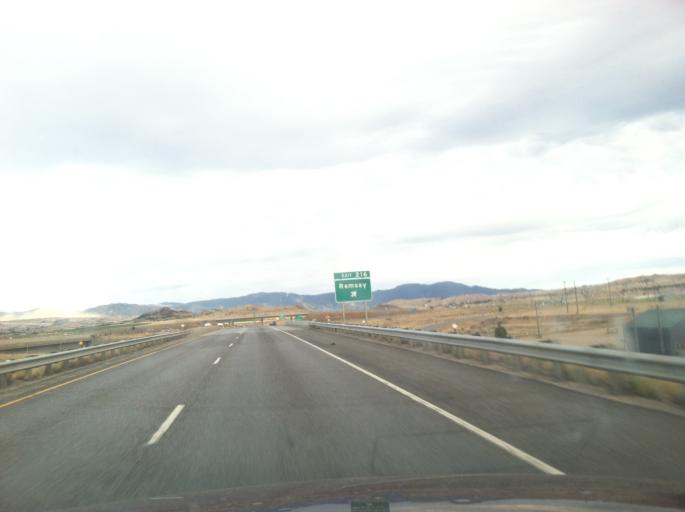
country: US
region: Montana
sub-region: Silver Bow County
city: Butte-Silver Bow (Balance)
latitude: 46.0099
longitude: -112.6910
